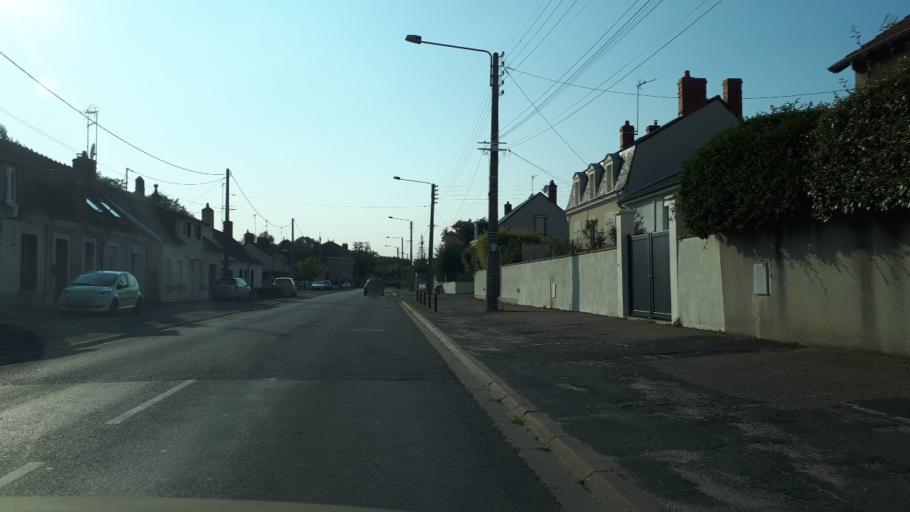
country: FR
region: Centre
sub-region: Departement du Cher
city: Vierzon
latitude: 47.2181
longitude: 2.0961
